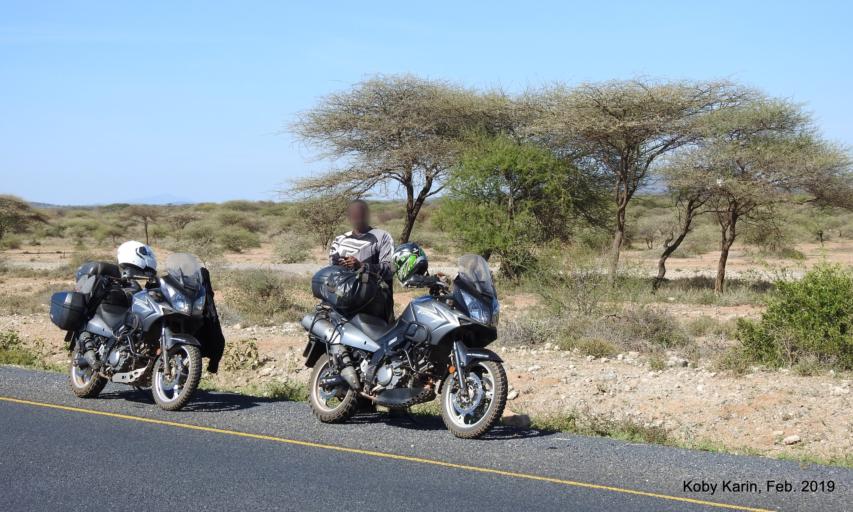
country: TZ
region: Arusha
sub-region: Longido District
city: Longido
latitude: -2.8359
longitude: 36.7098
